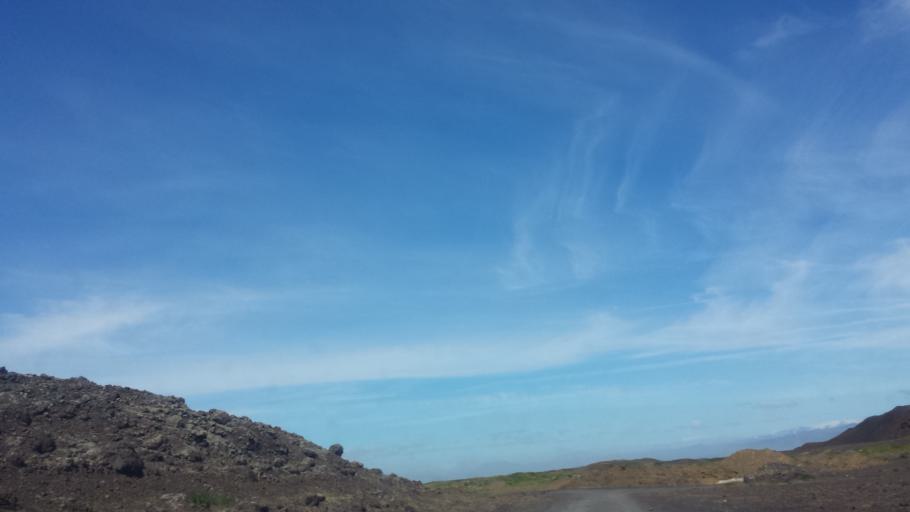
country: IS
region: South
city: Vestmannaeyjar
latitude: 63.4374
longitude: -20.2458
